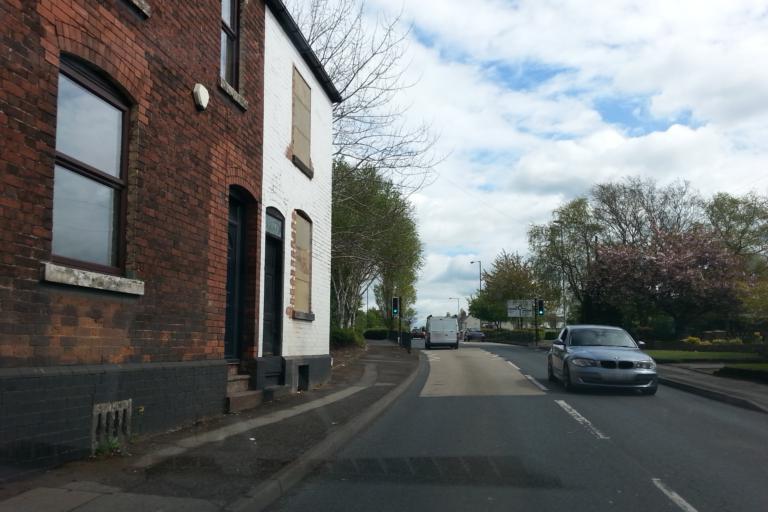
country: GB
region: England
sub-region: Staffordshire
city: Essington
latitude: 52.6104
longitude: -2.0422
